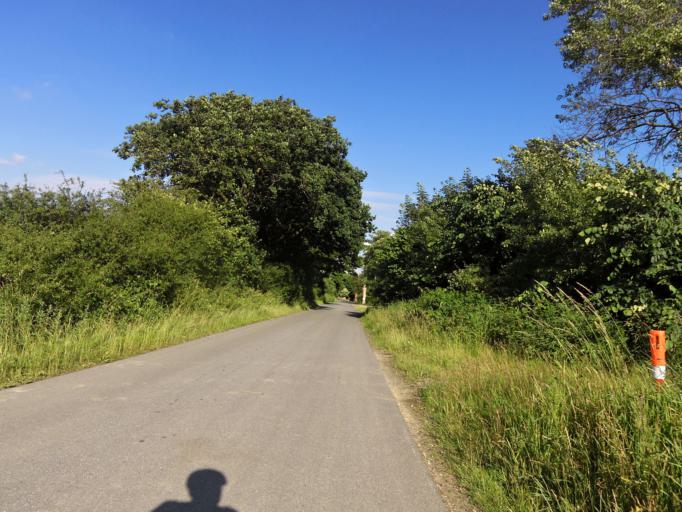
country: DK
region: South Denmark
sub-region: Vejen Kommune
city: Rodding
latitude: 55.3531
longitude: 9.0876
